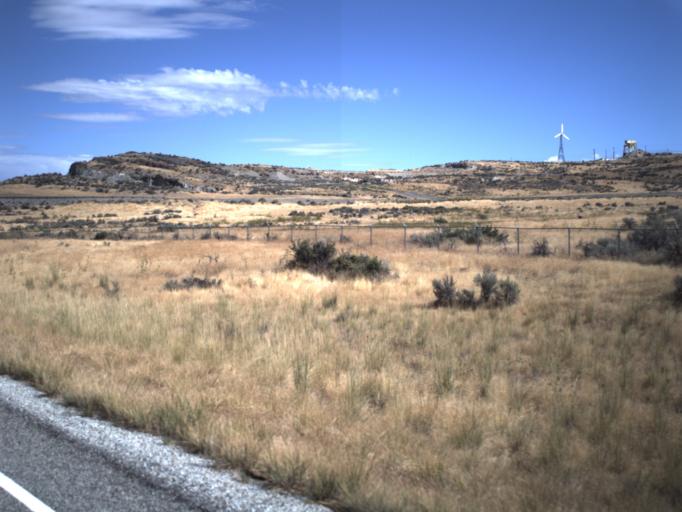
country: US
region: Utah
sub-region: Box Elder County
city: Tremonton
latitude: 41.6666
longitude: -112.4452
